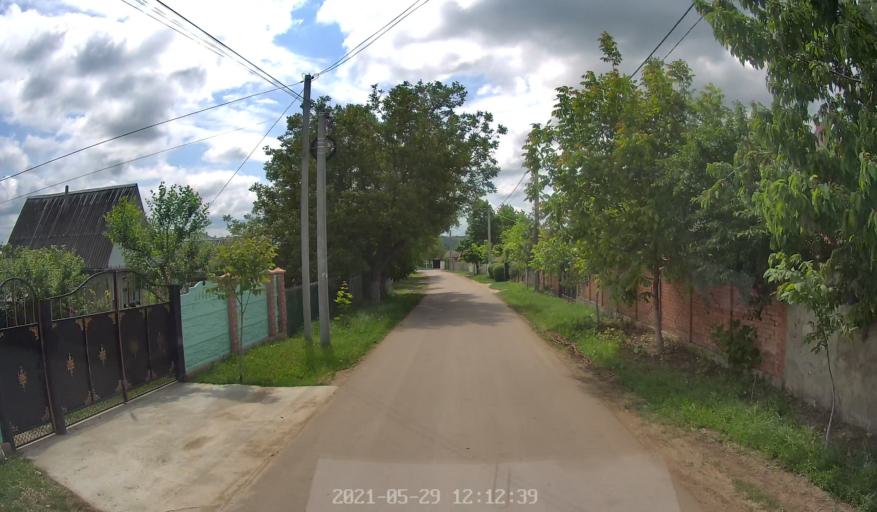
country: MD
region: Hincesti
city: Hincesti
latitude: 46.8784
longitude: 28.6320
